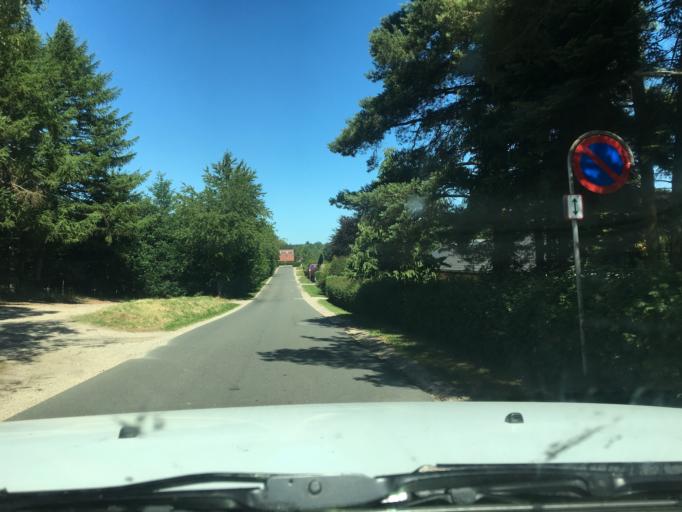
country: DK
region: Central Jutland
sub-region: Horsens Kommune
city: Braedstrup
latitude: 56.0119
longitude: 9.6826
